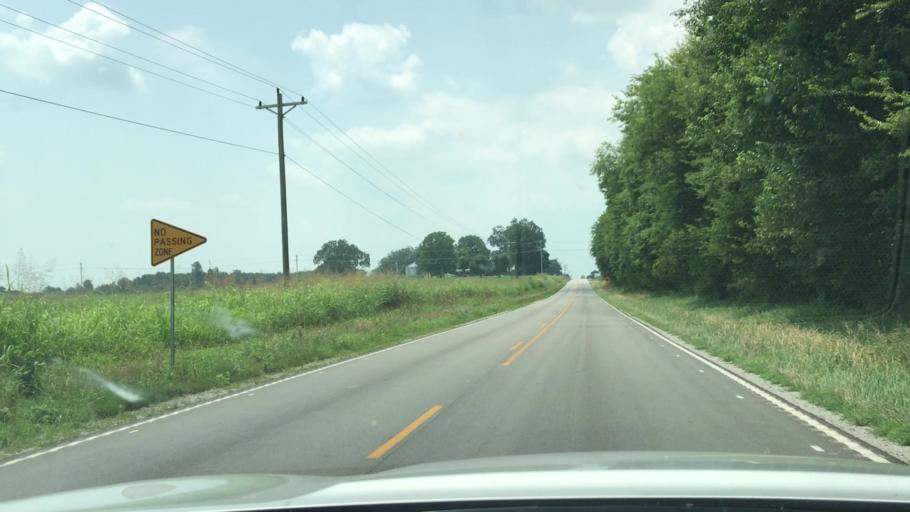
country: US
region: Kentucky
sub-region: Todd County
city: Guthrie
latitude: 36.6804
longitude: -87.1464
